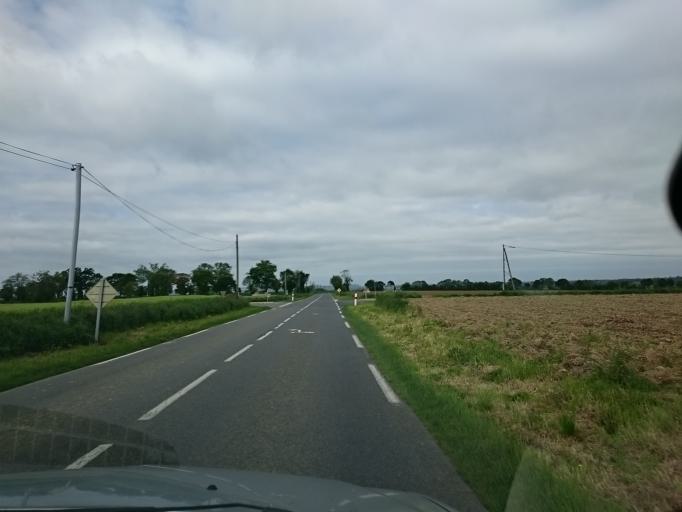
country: FR
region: Lower Normandy
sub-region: Departement de la Manche
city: Pontorson
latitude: 48.5547
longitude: -1.4416
